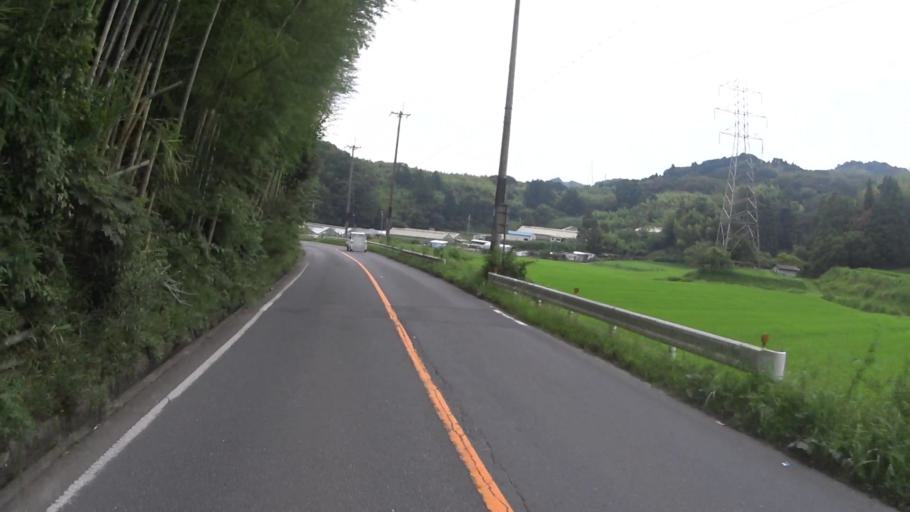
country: JP
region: Kyoto
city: Tanabe
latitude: 34.7864
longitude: 135.7499
